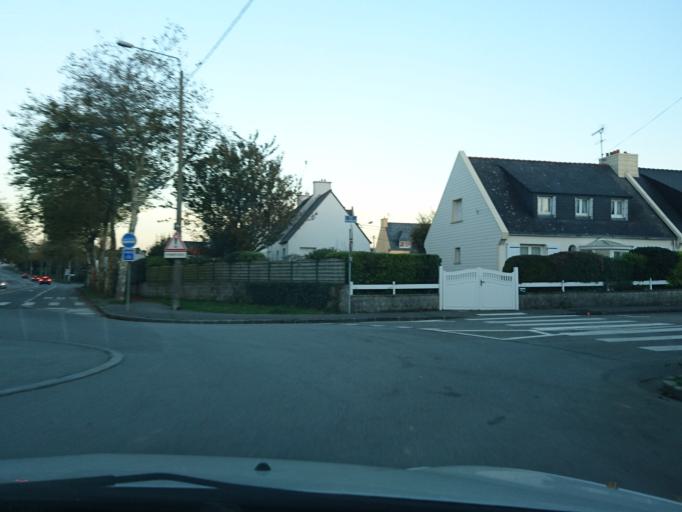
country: FR
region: Brittany
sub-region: Departement du Finistere
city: Brest
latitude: 48.4248
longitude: -4.4828
